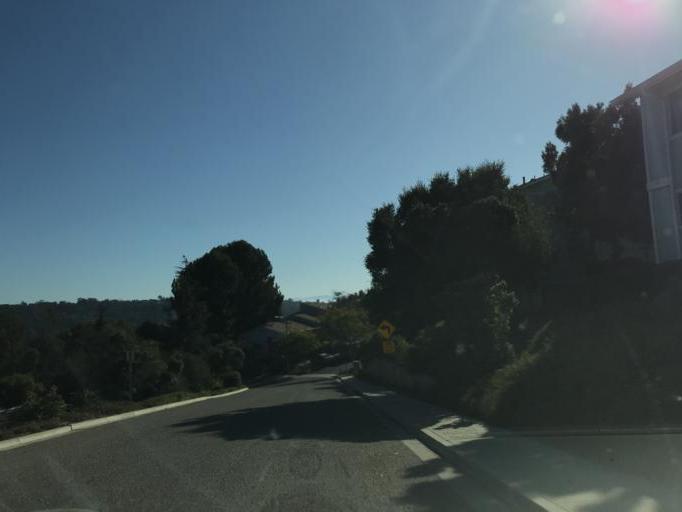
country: US
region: California
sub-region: Santa Barbara County
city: Goleta
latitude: 34.4474
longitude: -119.7811
